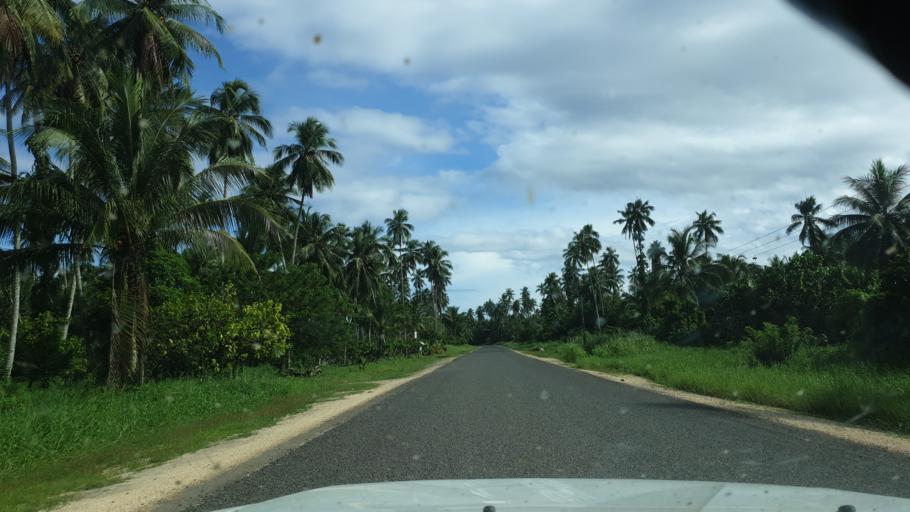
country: PG
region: Madang
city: Madang
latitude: -4.9858
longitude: 145.7871
